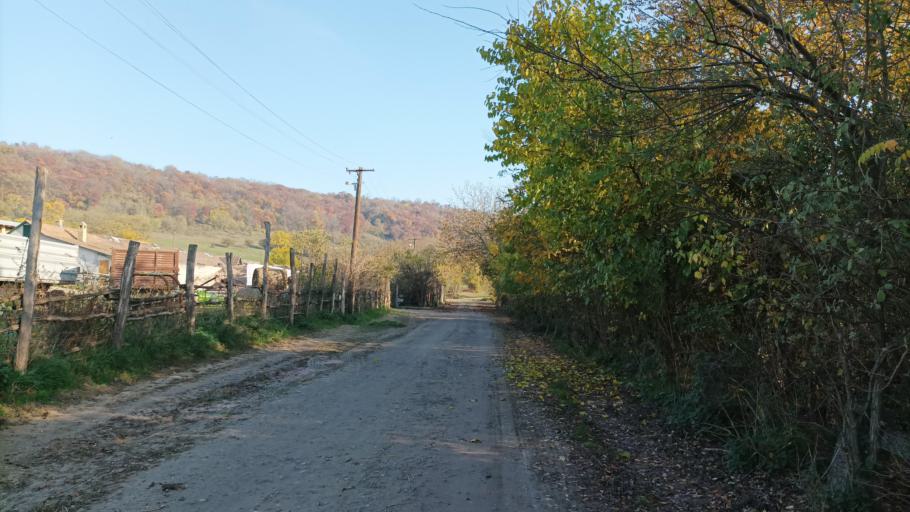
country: HU
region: Tolna
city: Szentgalpuszta
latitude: 46.3398
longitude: 18.6021
